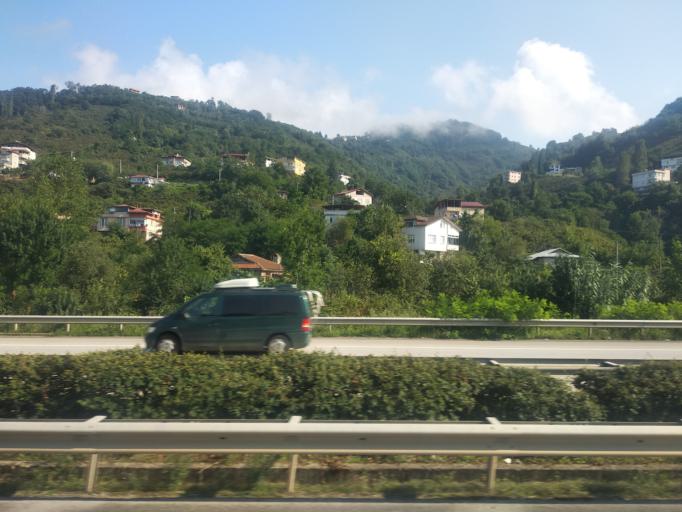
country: TR
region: Ordu
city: Ordu
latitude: 41.0157
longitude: 37.8418
